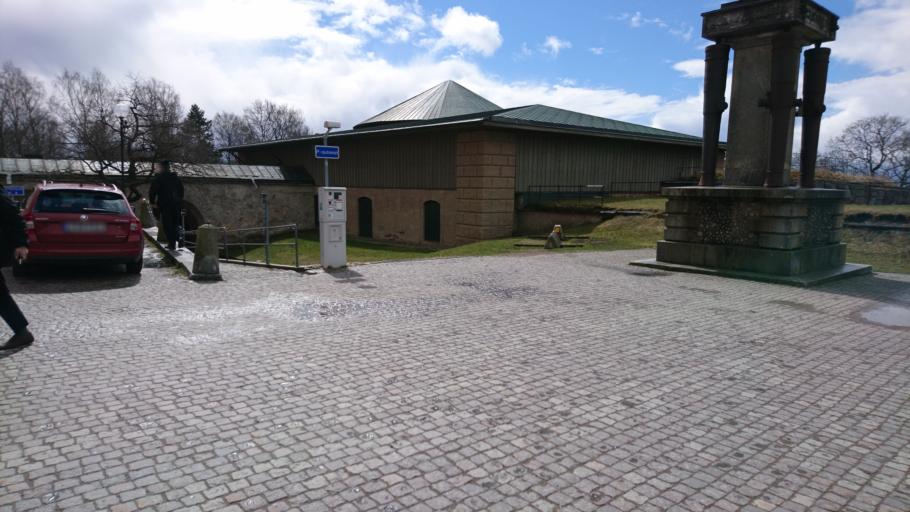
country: SE
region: Uppsala
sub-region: Uppsala Kommun
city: Uppsala
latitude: 59.8535
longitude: 17.6348
